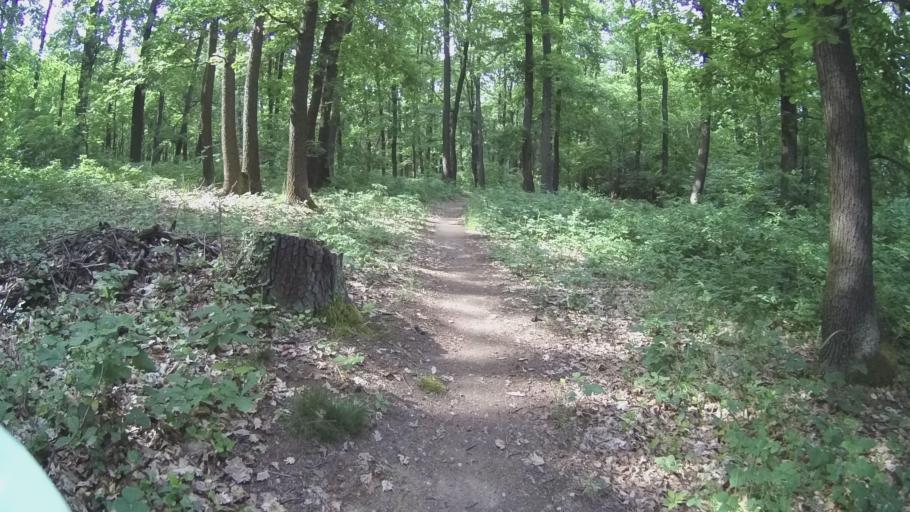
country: CZ
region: Central Bohemia
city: Zdiby
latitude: 50.2039
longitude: 14.4471
